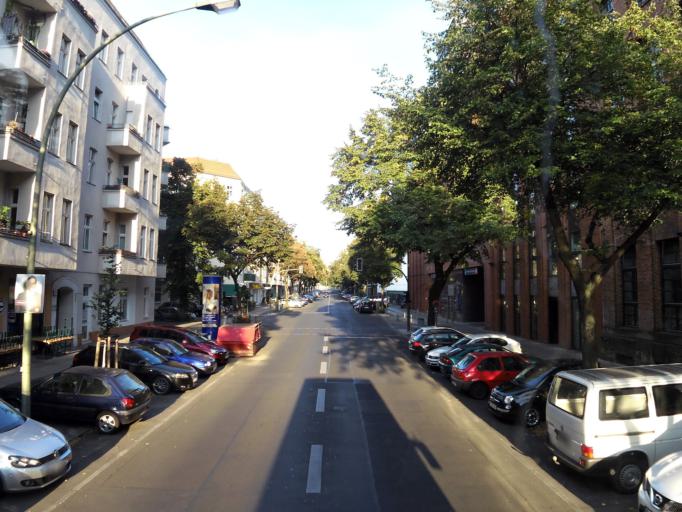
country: DE
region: Berlin
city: Moabit
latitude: 52.5215
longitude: 13.3241
